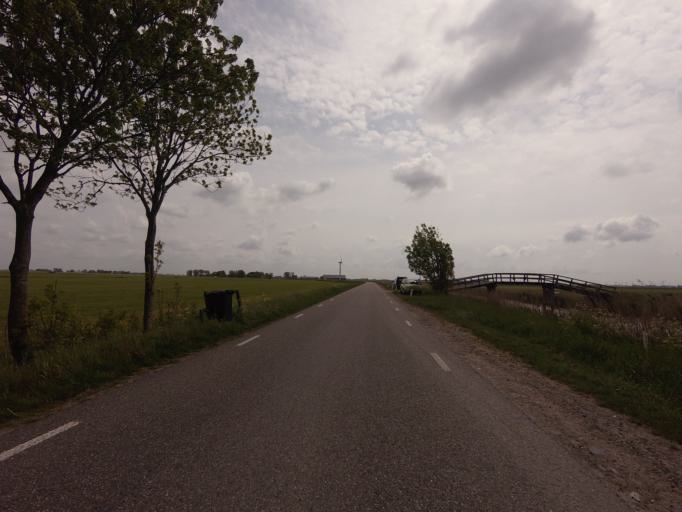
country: NL
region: Friesland
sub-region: Sudwest Fryslan
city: Bolsward
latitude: 53.1031
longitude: 5.5131
